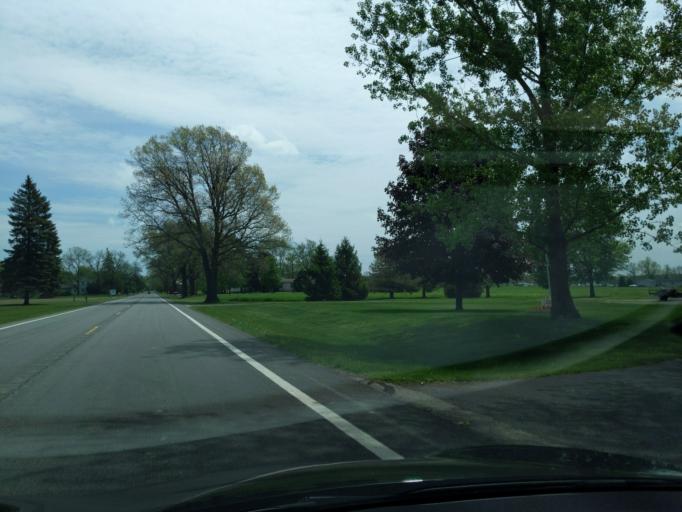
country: US
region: Michigan
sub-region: Ingham County
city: Stockbridge
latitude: 42.5089
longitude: -84.1564
